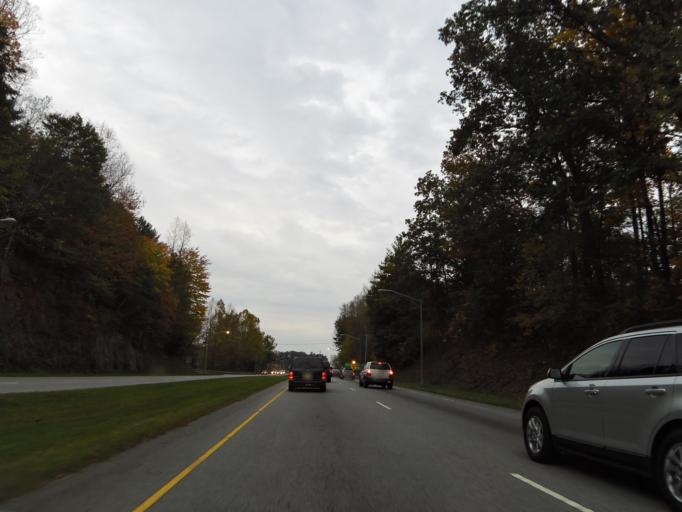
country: US
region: North Carolina
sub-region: Caldwell County
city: Lenoir
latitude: 35.9022
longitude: -81.5238
